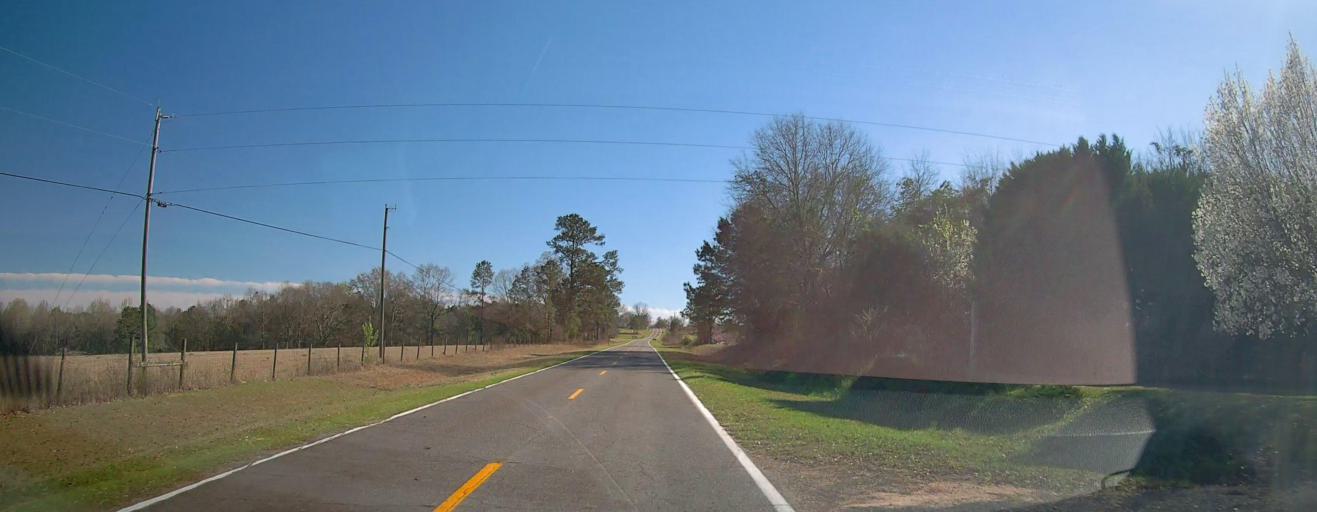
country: US
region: Georgia
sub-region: Peach County
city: Fort Valley
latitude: 32.6408
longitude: -83.8989
